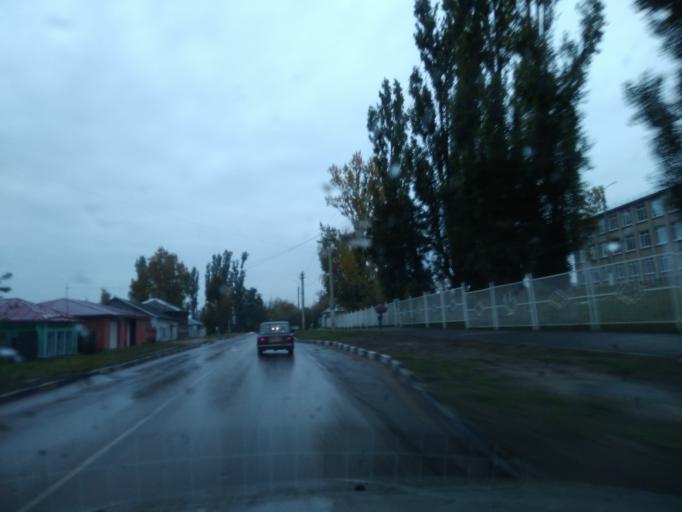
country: RU
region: Tula
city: Yefremov
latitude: 53.1410
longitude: 38.1063
